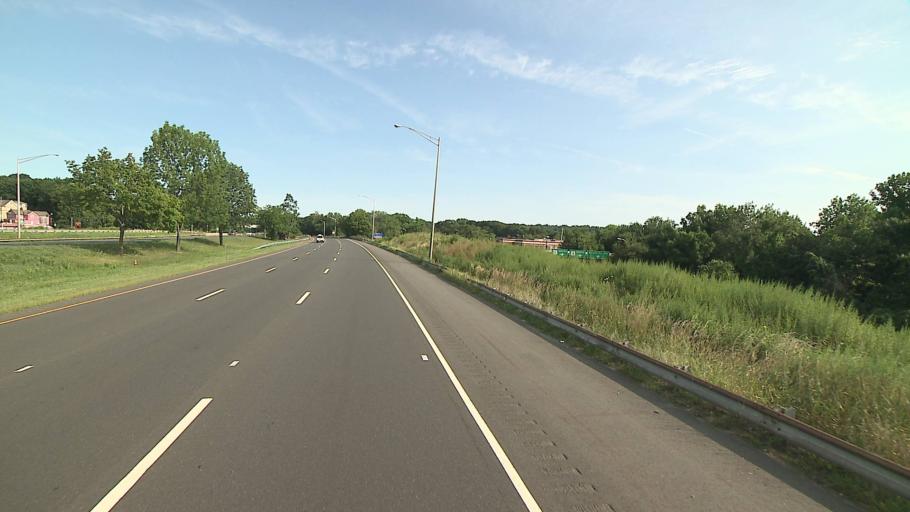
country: US
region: Connecticut
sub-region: Fairfield County
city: Norwalk
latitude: 41.1168
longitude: -73.4191
